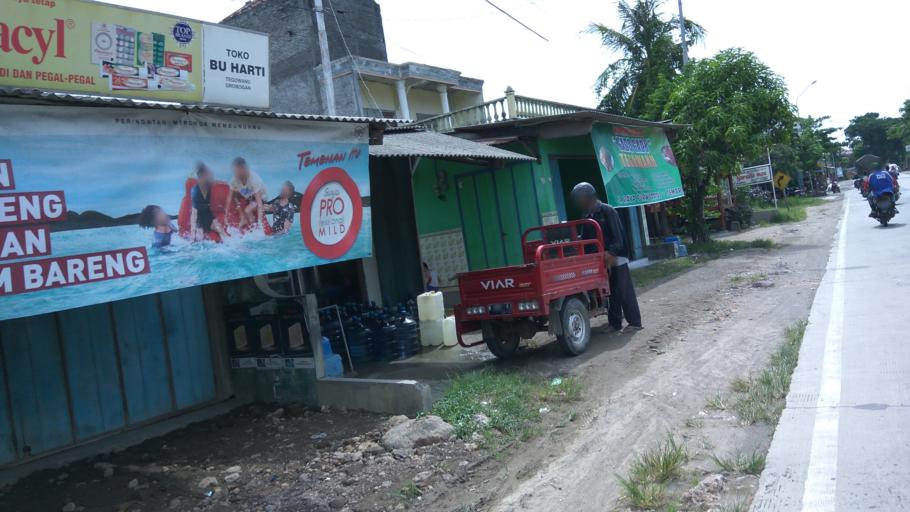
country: ID
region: Central Java
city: Mranggen
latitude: -7.0497
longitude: 110.6003
